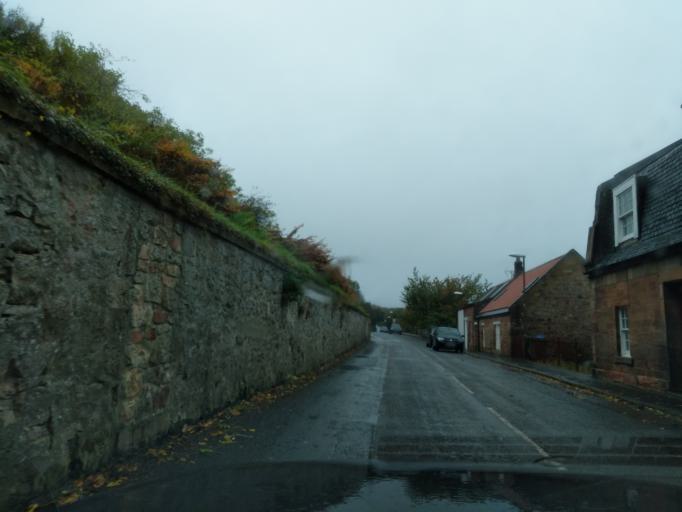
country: GB
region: Scotland
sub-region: East Lothian
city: Dunbar
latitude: 55.9572
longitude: -2.4476
